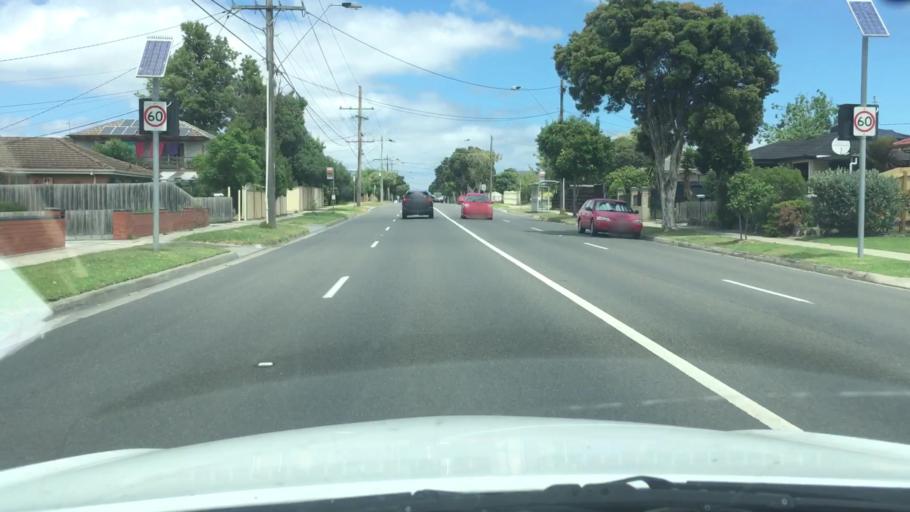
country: AU
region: Victoria
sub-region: Greater Dandenong
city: Keysborough
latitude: -37.9865
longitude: 145.1834
